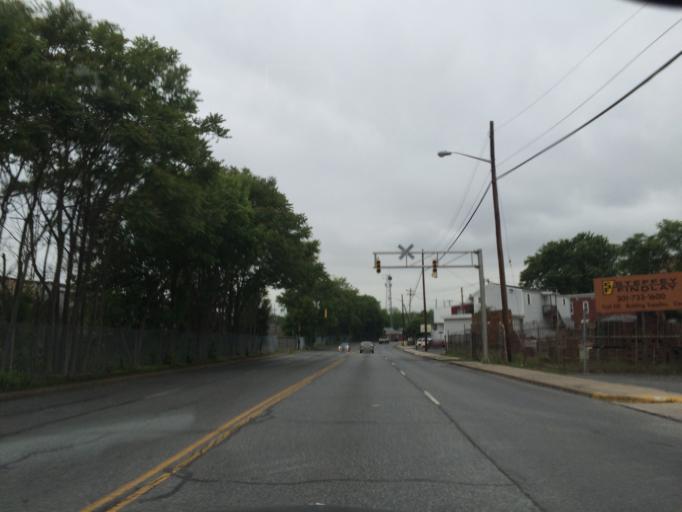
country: US
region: Maryland
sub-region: Washington County
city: Hagerstown
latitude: 39.6443
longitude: -77.7305
